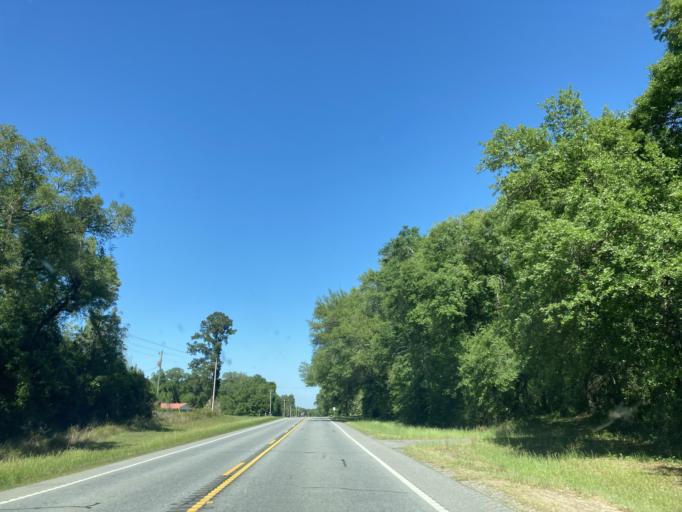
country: US
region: Georgia
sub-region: Baker County
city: Newton
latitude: 31.2877
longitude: -84.3606
